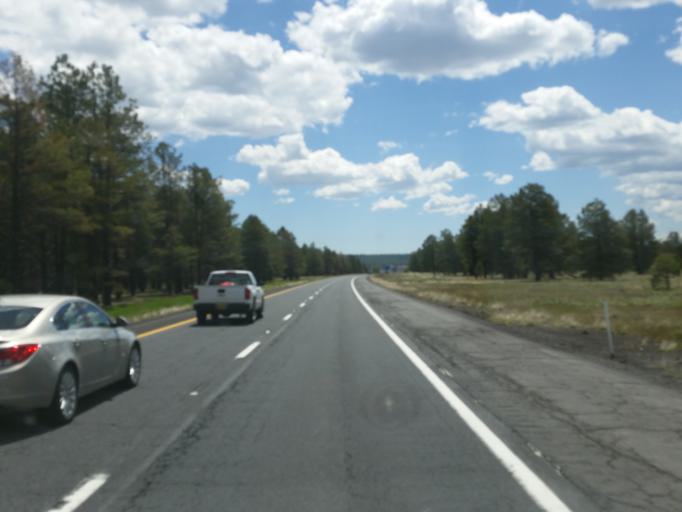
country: US
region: Arizona
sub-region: Coconino County
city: Parks
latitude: 35.2467
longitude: -111.8491
